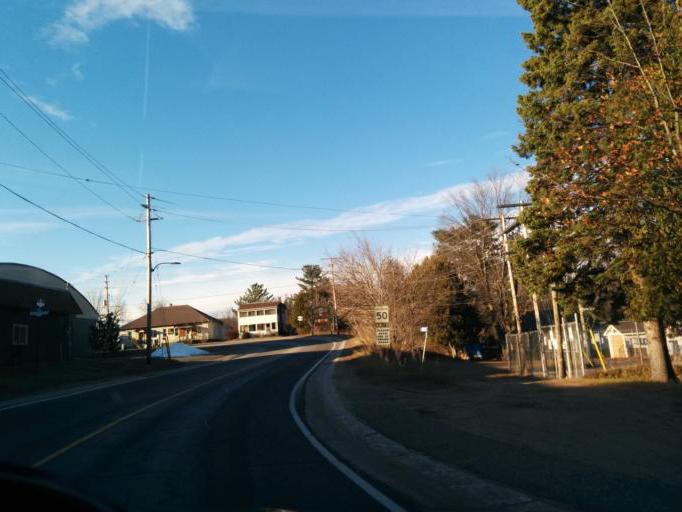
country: CA
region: Ontario
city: Bancroft
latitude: 45.0453
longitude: -78.5049
